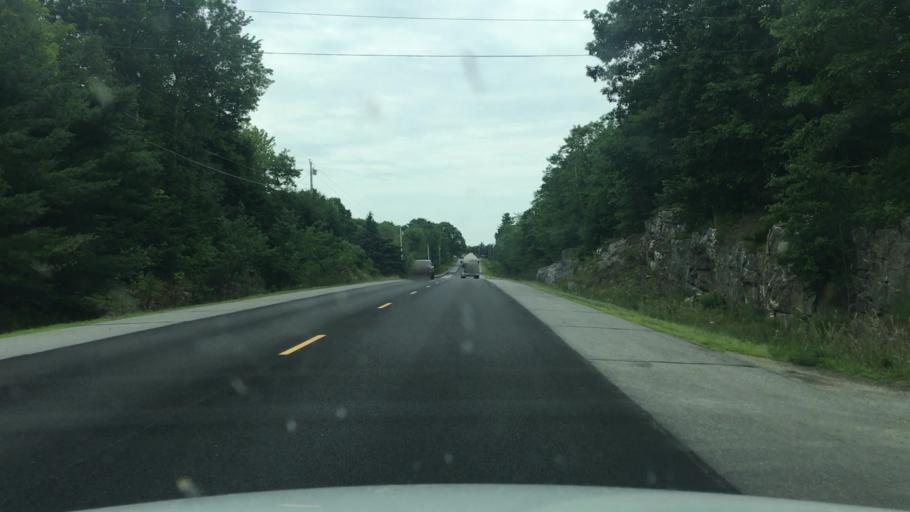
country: US
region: Maine
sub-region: Knox County
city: Washington
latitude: 44.3913
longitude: -69.3544
